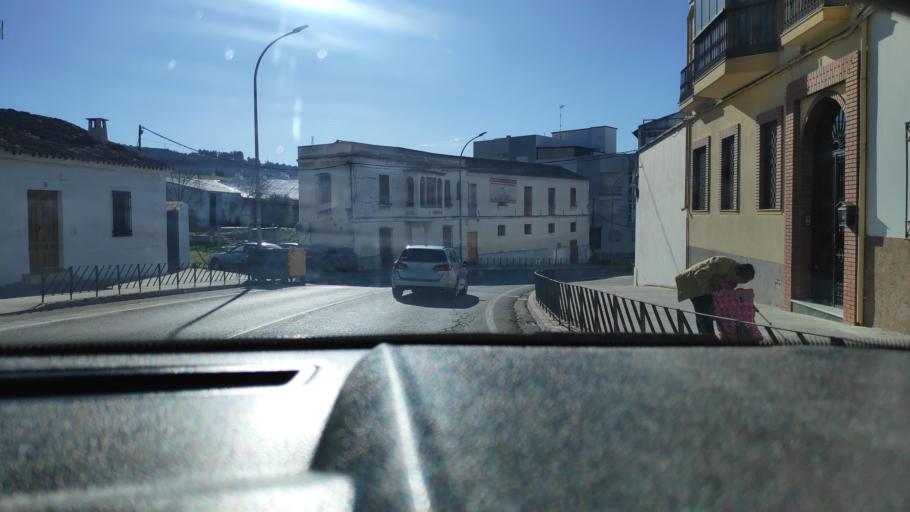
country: ES
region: Andalusia
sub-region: Province of Cordoba
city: Baena
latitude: 37.6149
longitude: -4.3212
